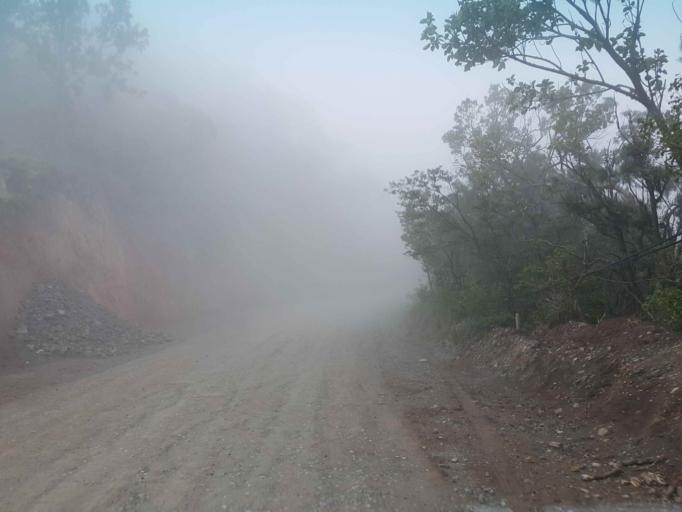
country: CR
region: Guanacaste
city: Juntas
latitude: 10.2912
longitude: -84.8325
